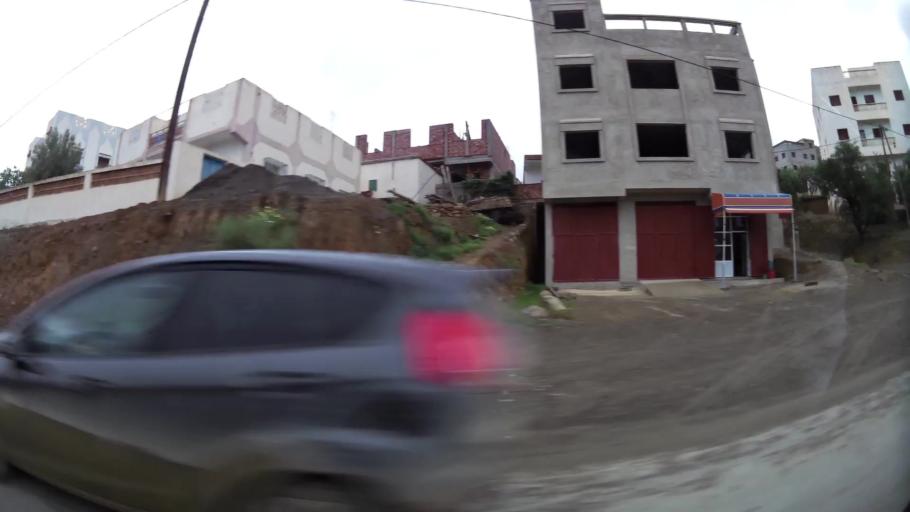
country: MA
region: Taza-Al Hoceima-Taounate
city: Imzourene
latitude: 34.9586
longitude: -3.8104
